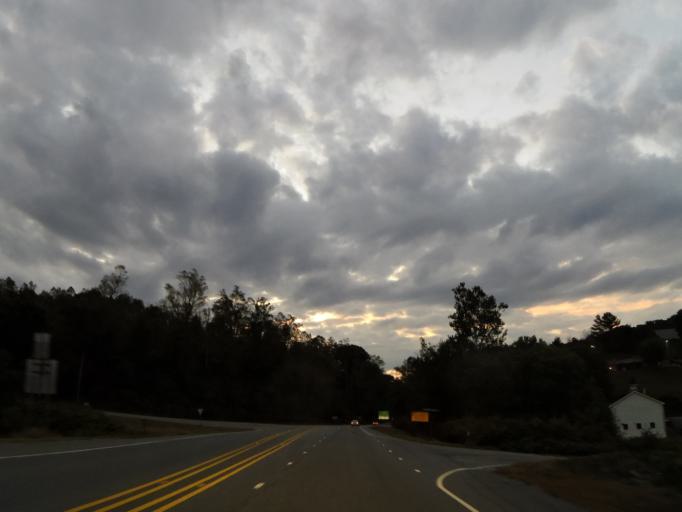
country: US
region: North Carolina
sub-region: Madison County
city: Marshall
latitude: 35.8141
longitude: -82.6902
